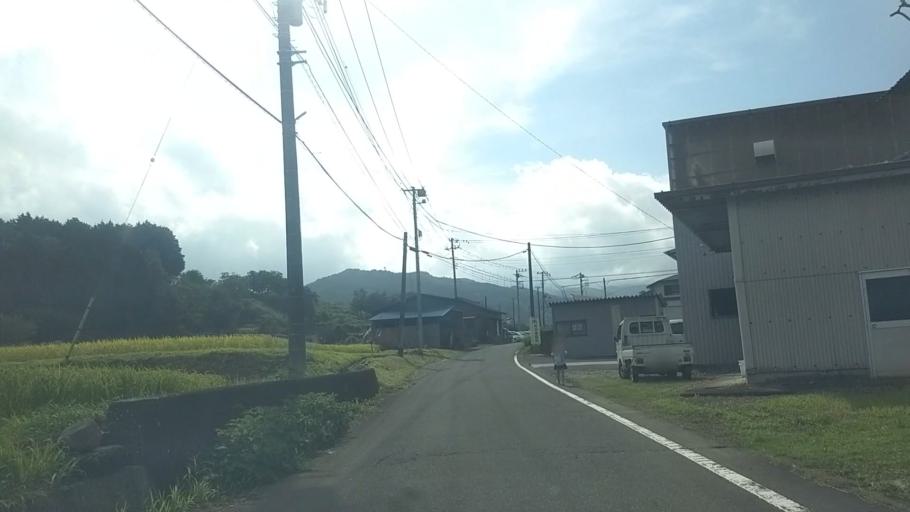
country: JP
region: Shizuoka
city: Heda
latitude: 34.9695
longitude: 138.9133
